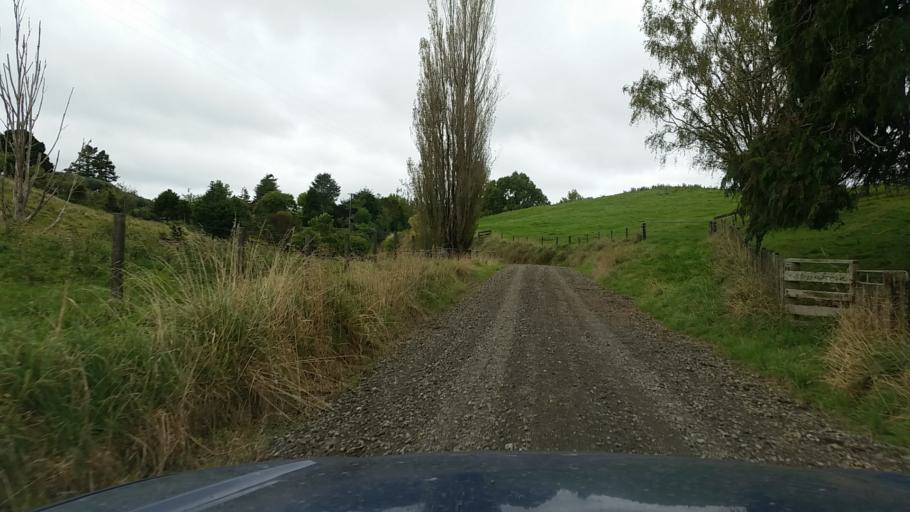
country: NZ
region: Taranaki
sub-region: South Taranaki District
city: Eltham
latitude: -39.2497
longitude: 174.4110
